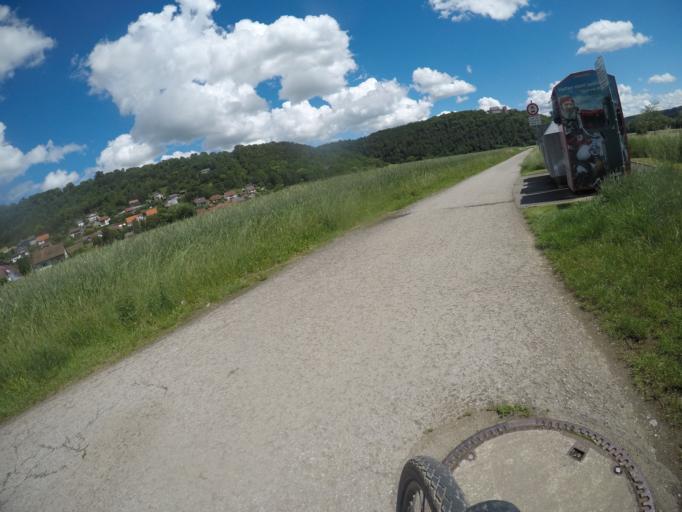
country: DE
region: Baden-Wuerttemberg
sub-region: Tuebingen Region
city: Haigerloch
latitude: 48.4459
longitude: 8.8060
